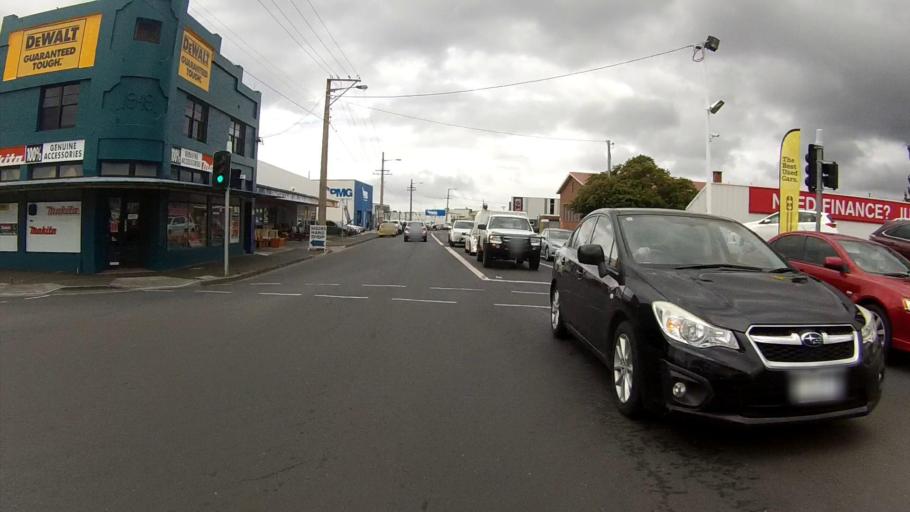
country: AU
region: Tasmania
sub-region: Glenorchy
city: Glenorchy
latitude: -42.8355
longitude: 147.2857
